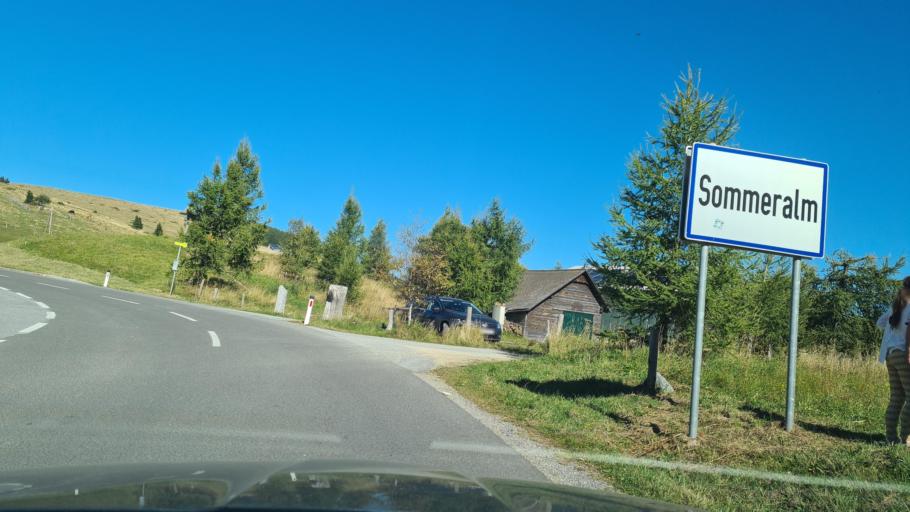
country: AT
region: Styria
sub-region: Politischer Bezirk Weiz
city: Gasen
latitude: 47.3450
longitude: 15.5523
